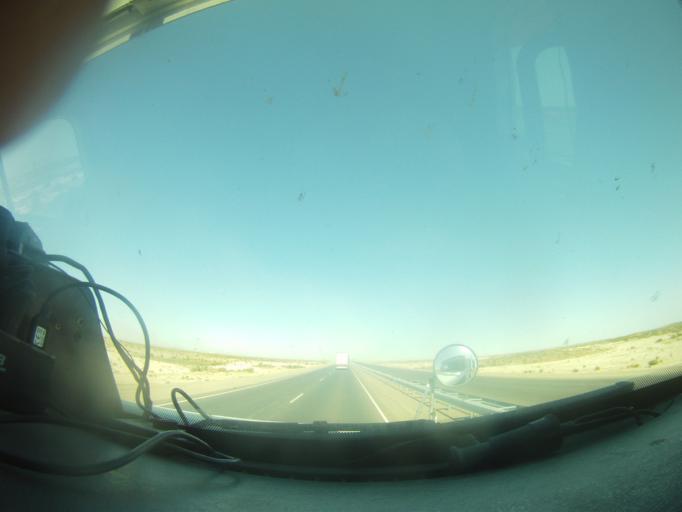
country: KZ
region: Qyzylorda
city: Belkol
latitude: 44.7980
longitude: 65.6275
